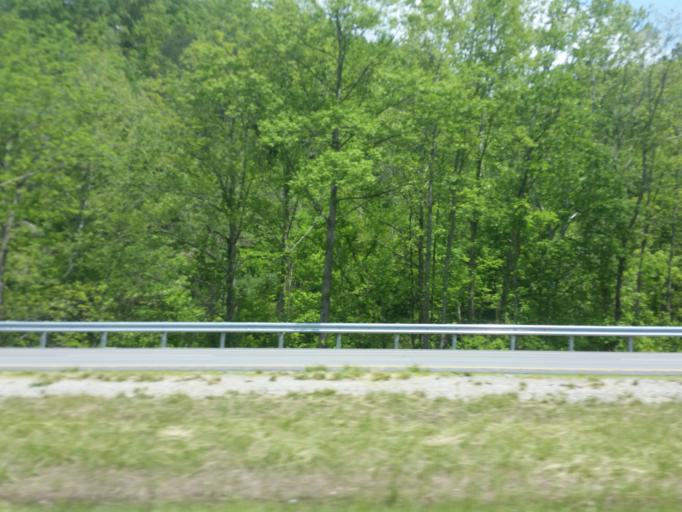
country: US
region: West Virginia
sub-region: Kanawha County
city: Sissonville
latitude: 38.6209
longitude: -81.6440
